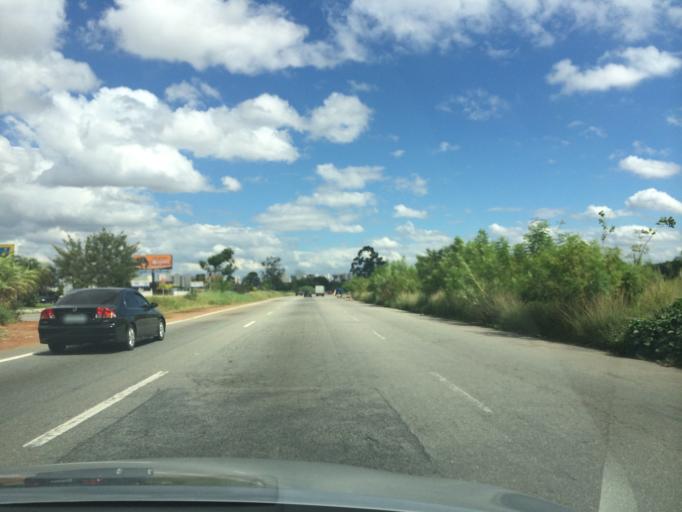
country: BR
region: Sao Paulo
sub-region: Guarulhos
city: Guarulhos
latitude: -23.5051
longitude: -46.5589
